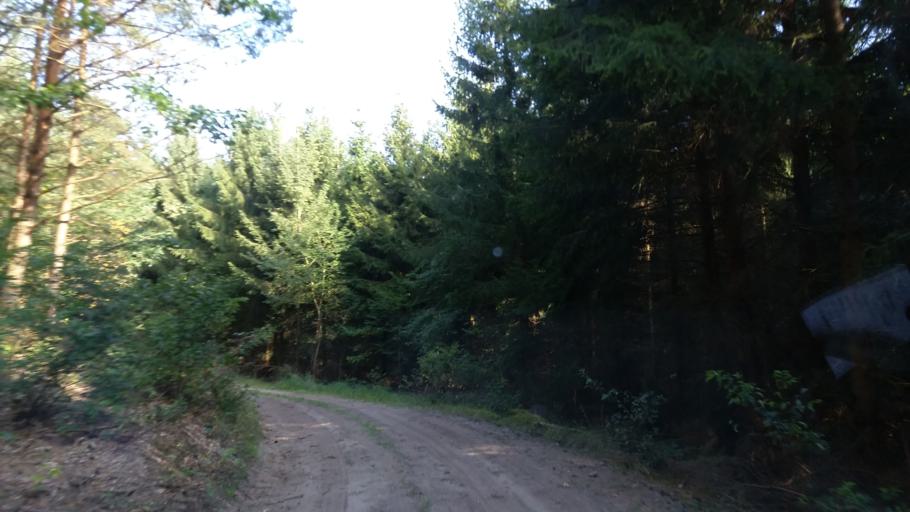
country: PL
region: West Pomeranian Voivodeship
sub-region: Powiat choszczenski
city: Choszczno
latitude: 53.2255
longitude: 15.4515
